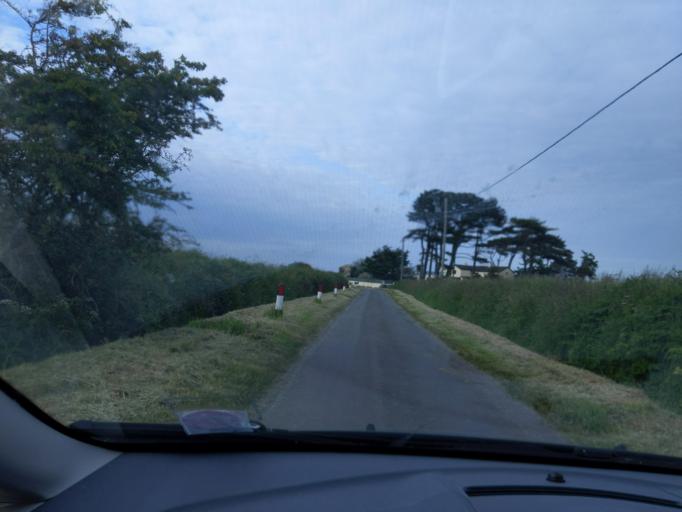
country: IM
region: Ramsey
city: Ramsey
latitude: 54.3913
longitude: -4.4465
